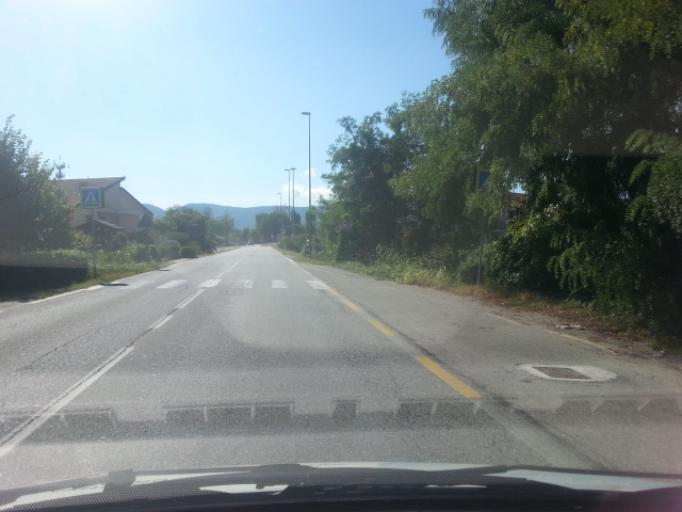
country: IT
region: Piedmont
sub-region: Provincia di Torino
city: Rivalta di Torino
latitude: 45.0293
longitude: 7.5285
